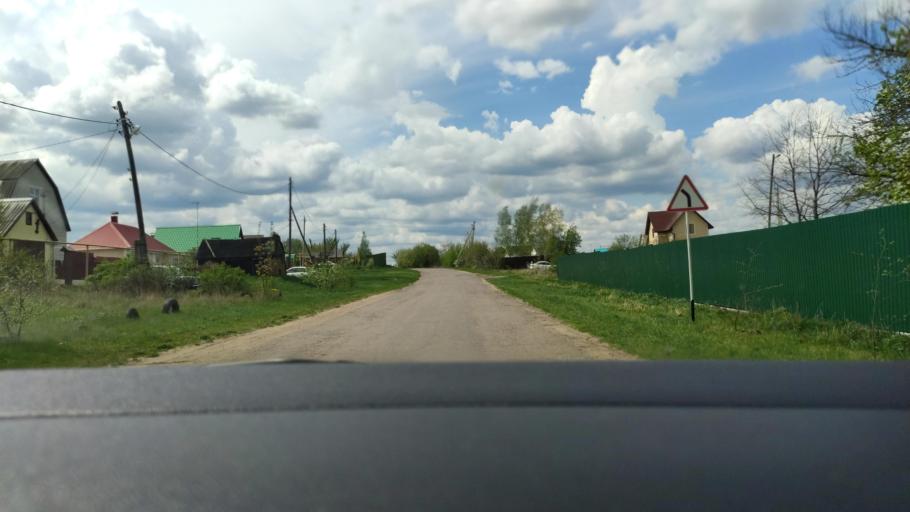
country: RU
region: Voronezj
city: Semiluki
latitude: 51.7827
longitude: 39.0092
